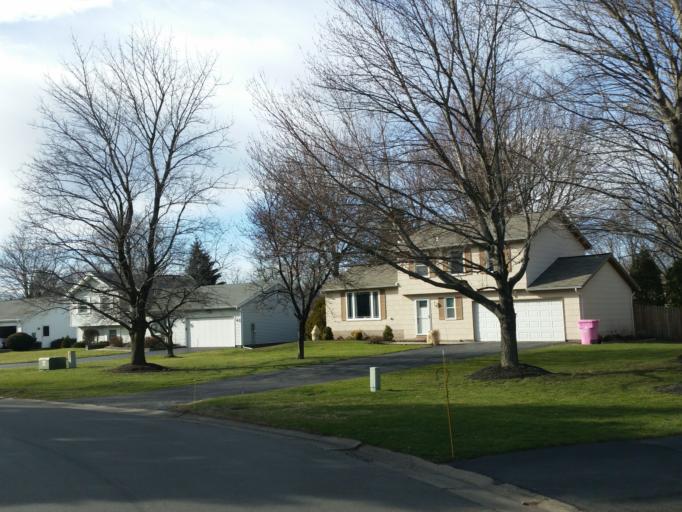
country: US
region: New York
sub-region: Monroe County
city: North Gates
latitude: 43.1243
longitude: -77.7366
